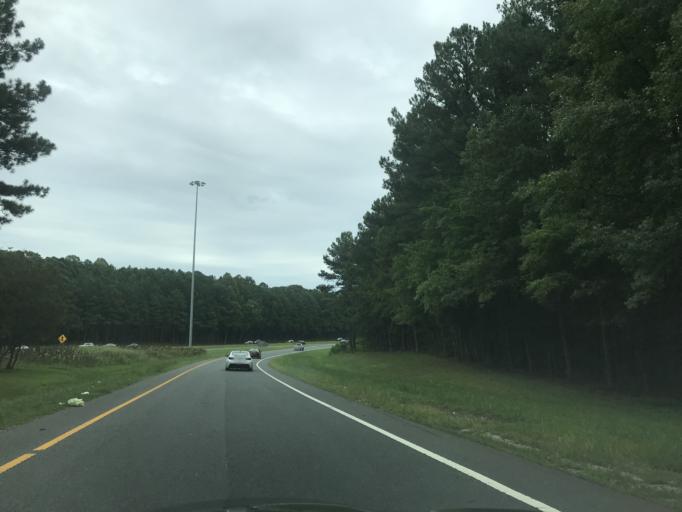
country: US
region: North Carolina
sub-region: Wake County
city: Cary
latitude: 35.7784
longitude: -78.7491
